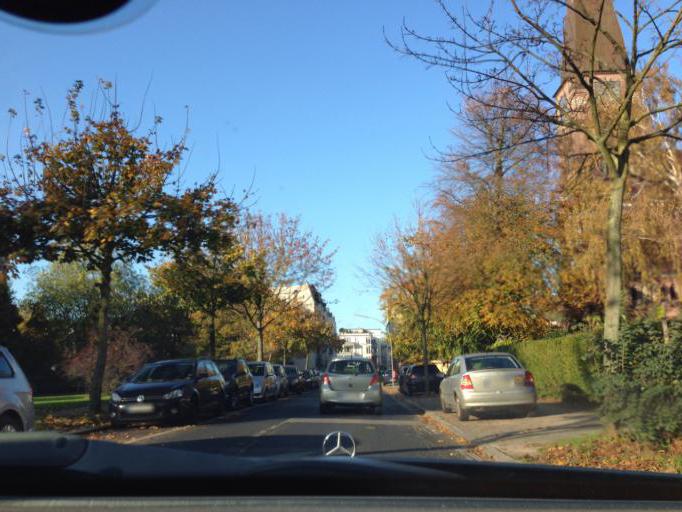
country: DE
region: Hamburg
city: Marienthal
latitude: 53.5788
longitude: 10.0864
